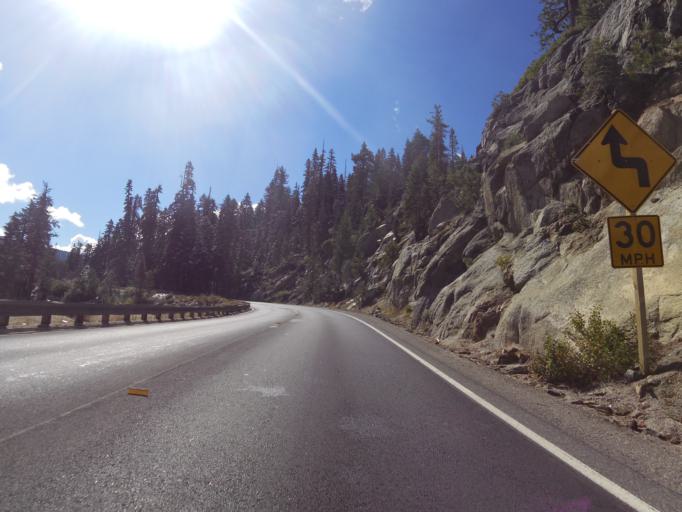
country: US
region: California
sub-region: El Dorado County
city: South Lake Tahoe
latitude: 38.8374
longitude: -120.0376
